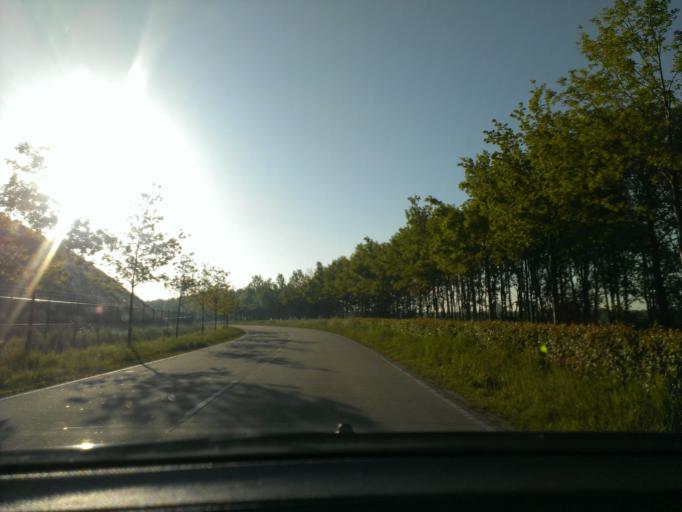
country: NL
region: Gelderland
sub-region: Gemeente Voorst
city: Twello
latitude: 52.1982
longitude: 6.0757
